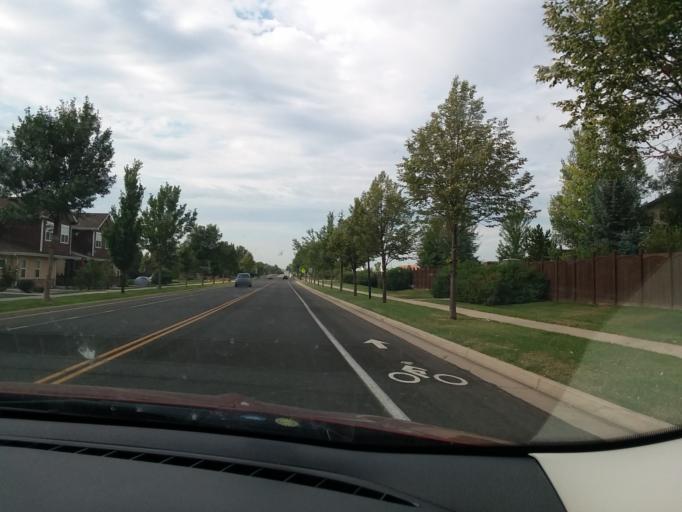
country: US
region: Colorado
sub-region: Larimer County
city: Fort Collins
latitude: 40.5068
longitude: -105.0199
